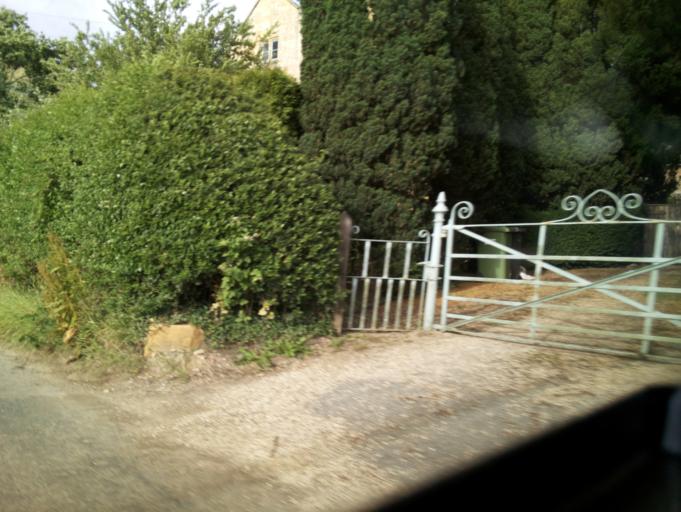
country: GB
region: England
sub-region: Gloucestershire
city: Chipping Campden
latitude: 52.0380
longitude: -1.7326
